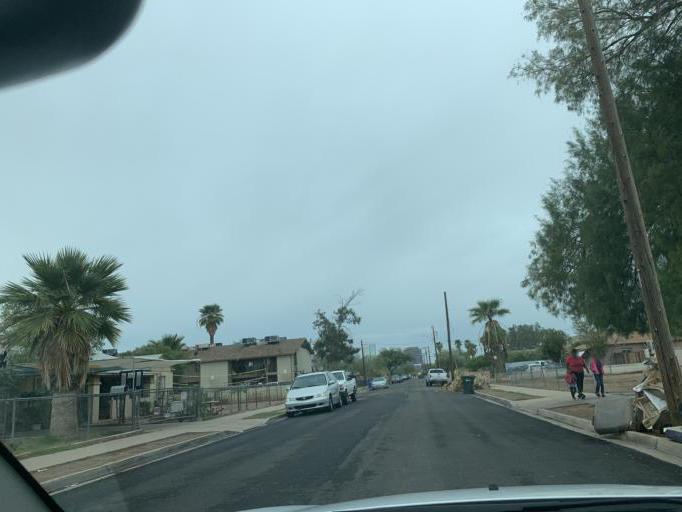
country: US
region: Arizona
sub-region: Maricopa County
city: Phoenix
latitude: 33.4527
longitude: -112.0496
